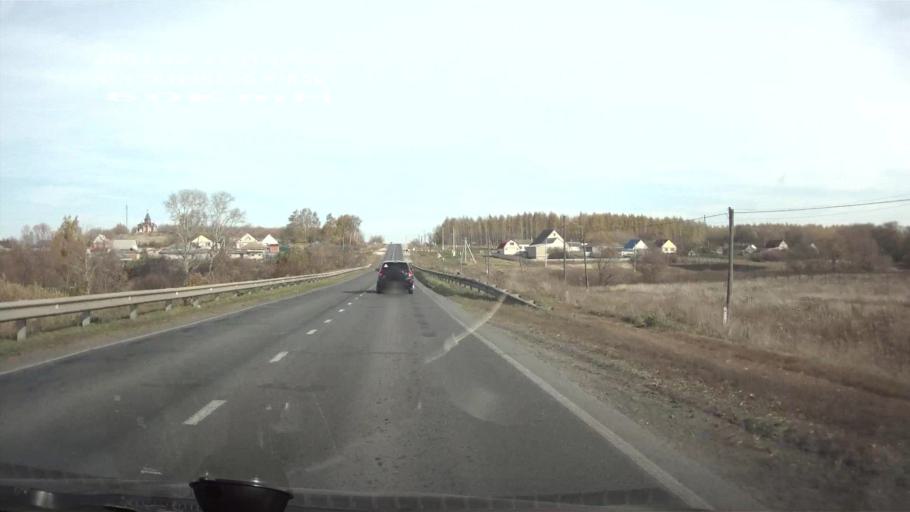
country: RU
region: Mordoviya
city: Atyashevo
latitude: 54.5615
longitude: 45.9785
